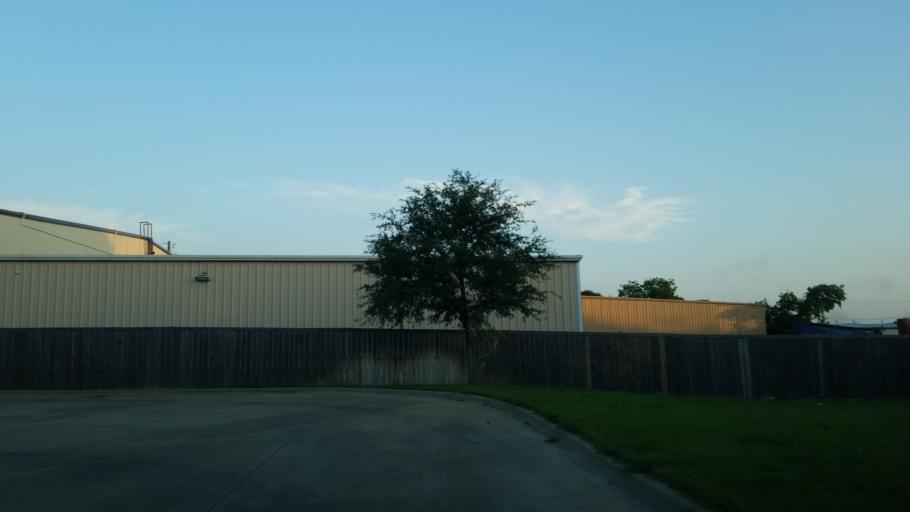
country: US
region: Texas
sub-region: Dallas County
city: Farmers Branch
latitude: 32.8876
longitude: -96.8890
